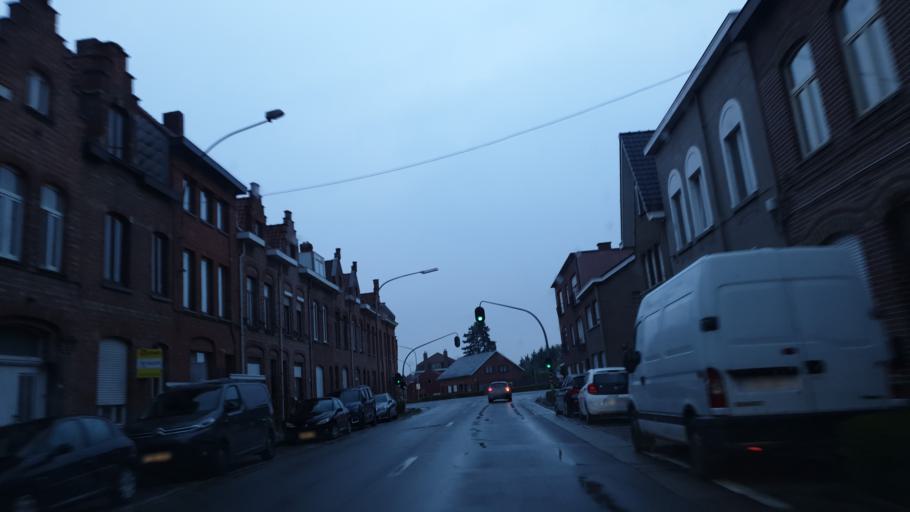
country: BE
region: Flanders
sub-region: Provincie West-Vlaanderen
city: Ieper
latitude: 50.8580
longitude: 2.8911
